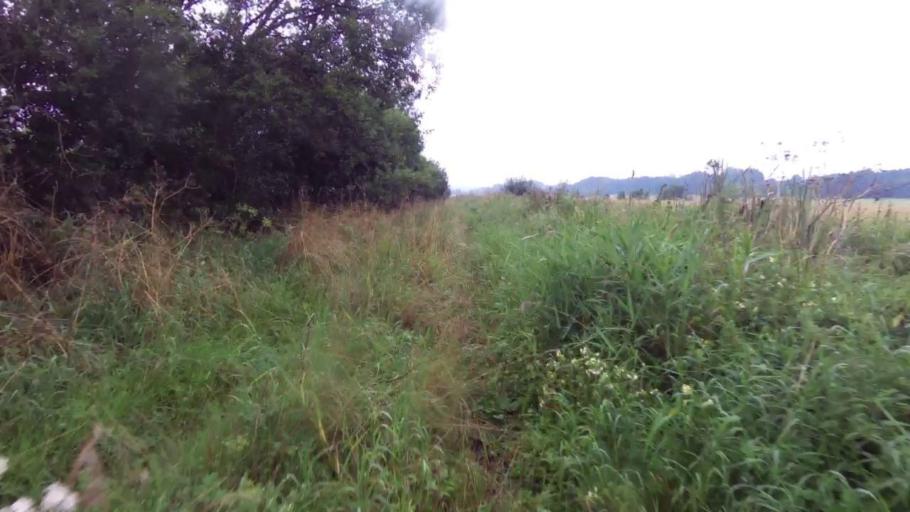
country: PL
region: West Pomeranian Voivodeship
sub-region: Powiat choszczenski
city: Choszczno
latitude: 53.2501
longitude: 15.4109
